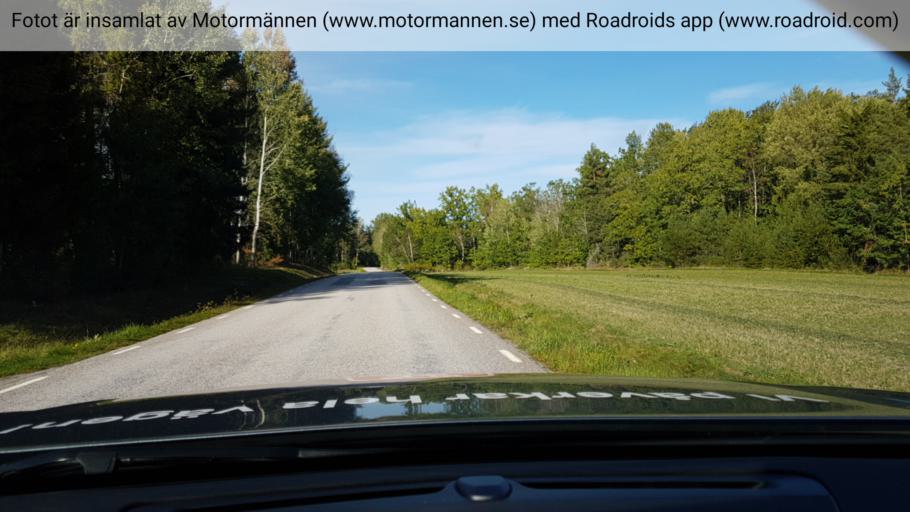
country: SE
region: OEstergoetland
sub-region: Valdemarsviks Kommun
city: Valdemarsvik
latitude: 58.0854
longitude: 16.6391
